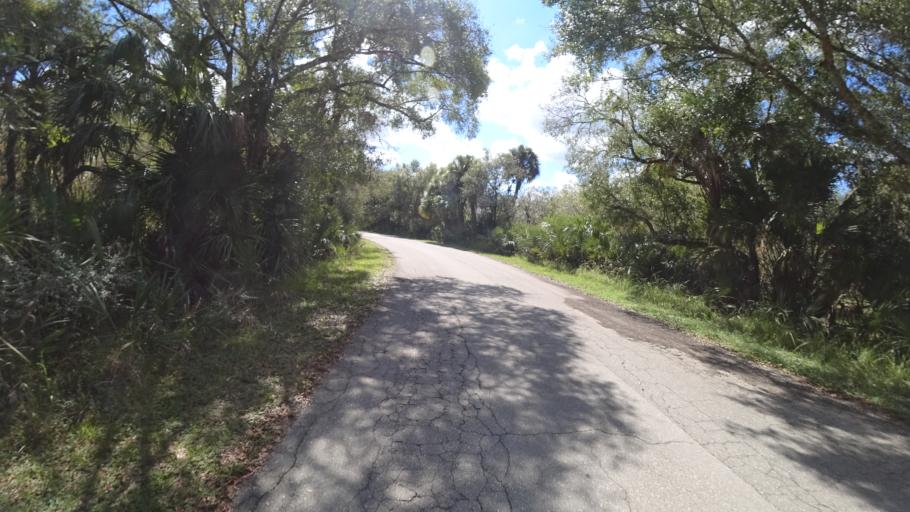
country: US
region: Florida
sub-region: Sarasota County
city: Lake Sarasota
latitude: 27.2806
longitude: -82.2612
